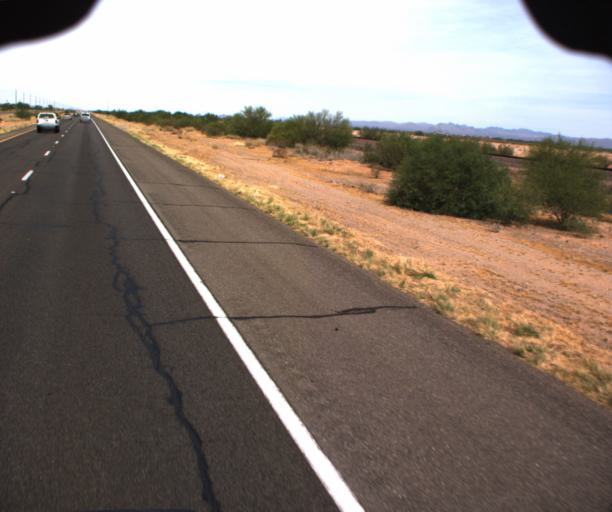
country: US
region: Arizona
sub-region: Maricopa County
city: Sun City West
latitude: 33.7071
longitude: -112.4376
